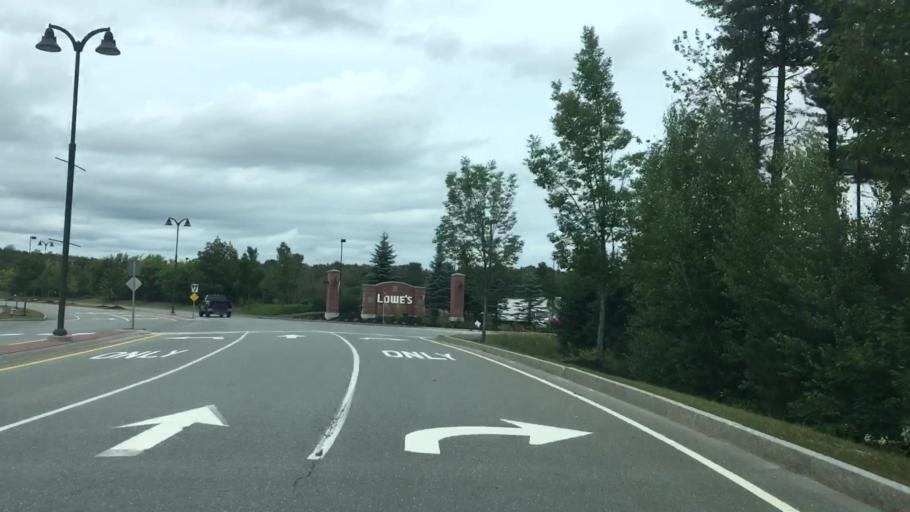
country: US
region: Maine
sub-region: Cumberland County
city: South Portland Gardens
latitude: 43.6225
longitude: -70.3392
